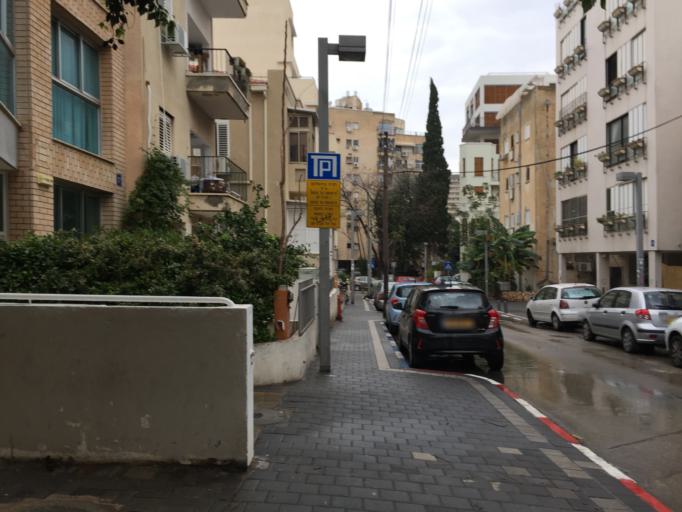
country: IL
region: Tel Aviv
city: Tel Aviv
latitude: 32.0699
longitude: 34.7734
